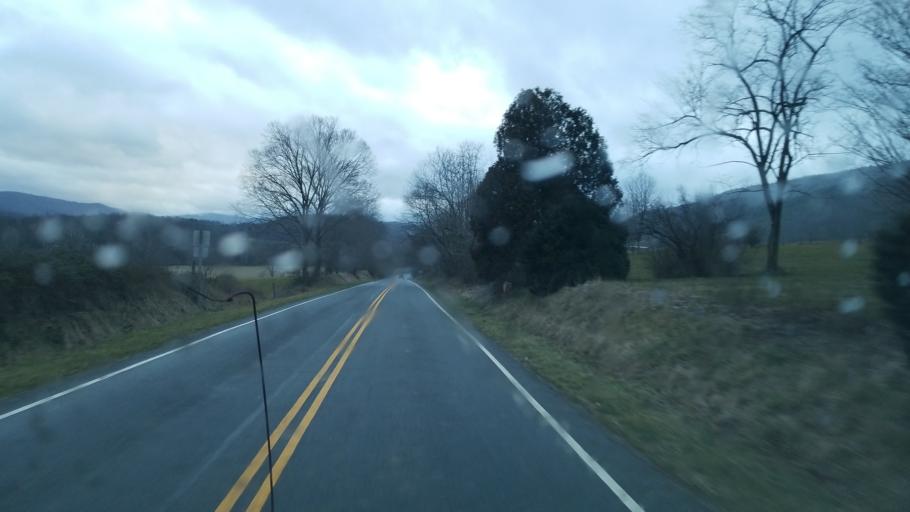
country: US
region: Virginia
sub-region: Giles County
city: Narrows
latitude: 37.2001
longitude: -80.8242
